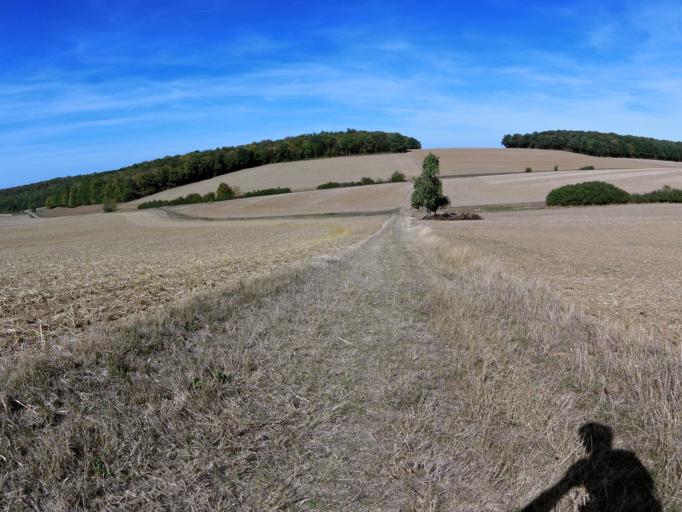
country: DE
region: Bavaria
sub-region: Regierungsbezirk Unterfranken
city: Eisingen
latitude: 49.7629
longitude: 9.8330
